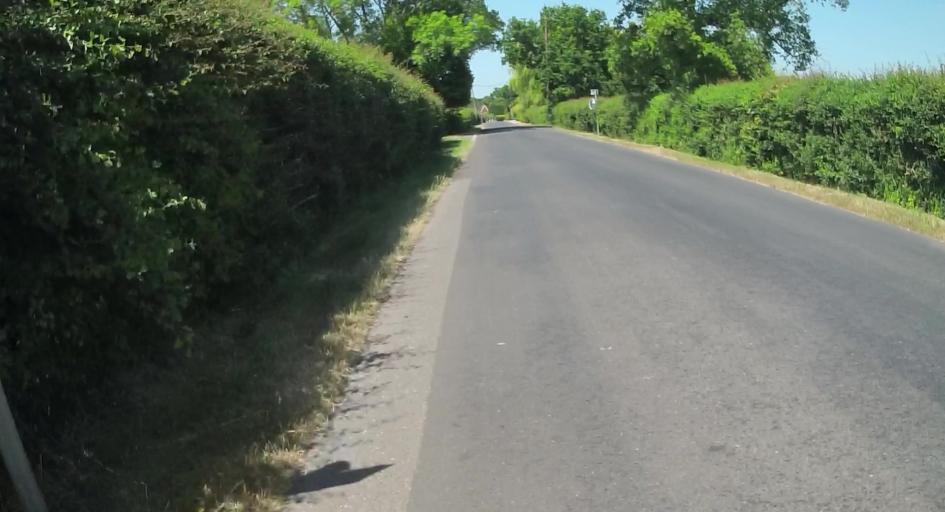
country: GB
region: England
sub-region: Hampshire
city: Tadley
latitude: 51.3243
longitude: -1.1734
